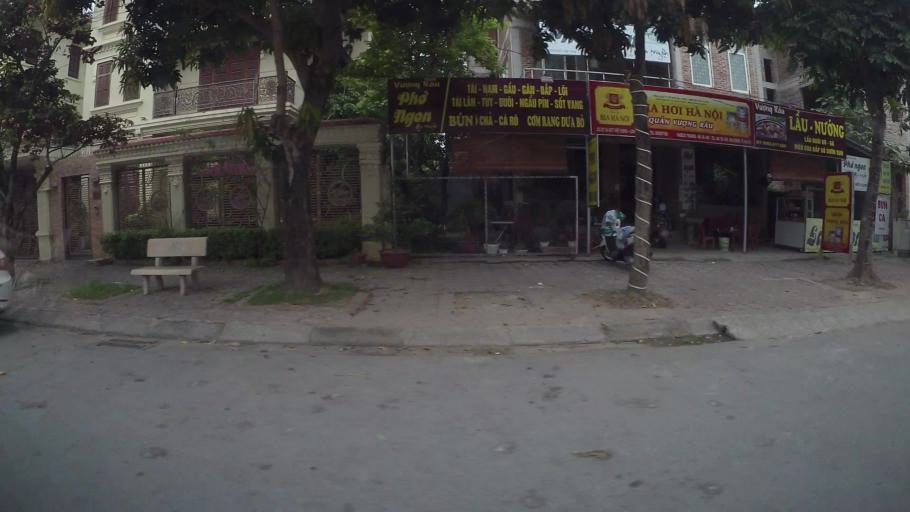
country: VN
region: Ha Noi
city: Trau Quy
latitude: 21.0671
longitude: 105.9099
